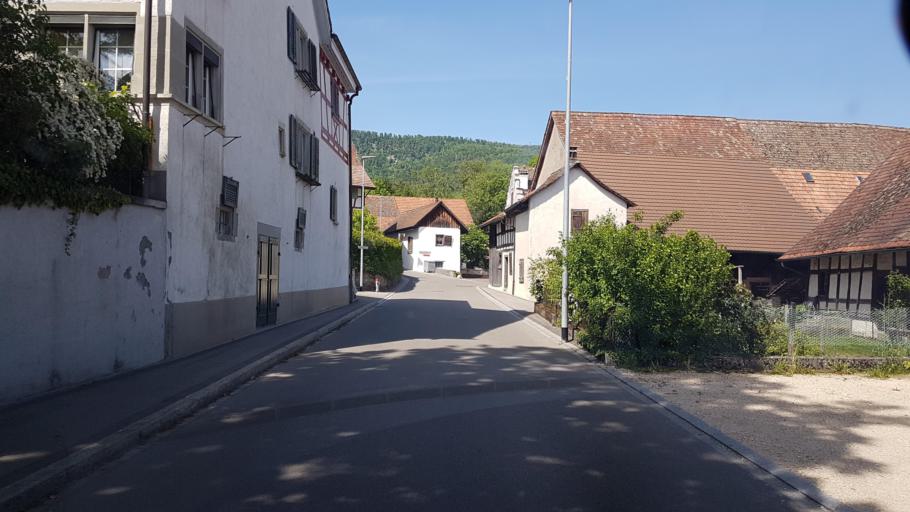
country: CH
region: Zurich
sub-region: Bezirk Dielsdorf
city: Otelfingen
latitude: 47.4629
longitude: 8.3872
